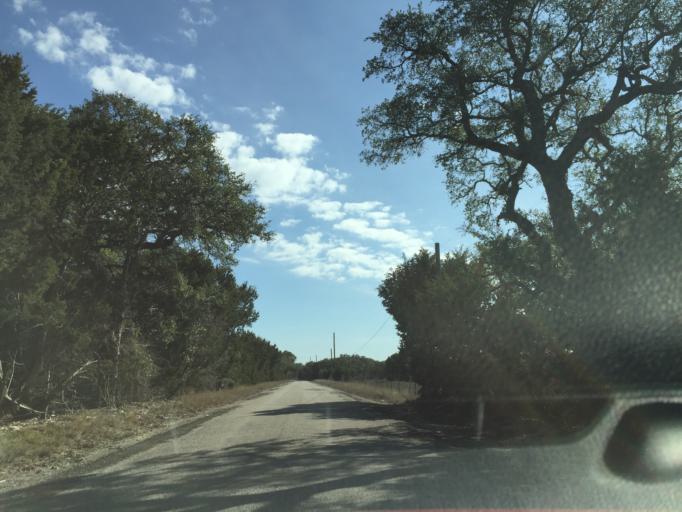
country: US
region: Texas
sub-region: Williamson County
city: Florence
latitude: 30.7769
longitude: -97.8905
